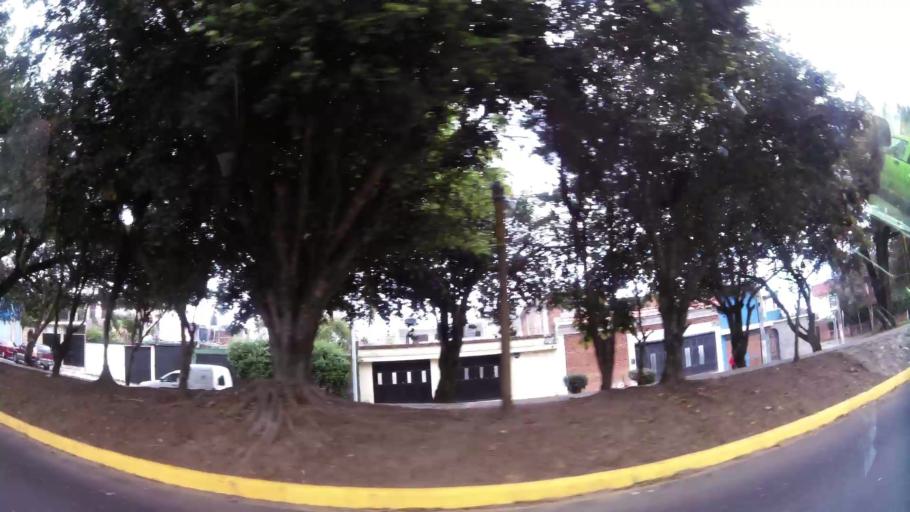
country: GT
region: Guatemala
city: Guatemala City
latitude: 14.6319
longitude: -90.5512
